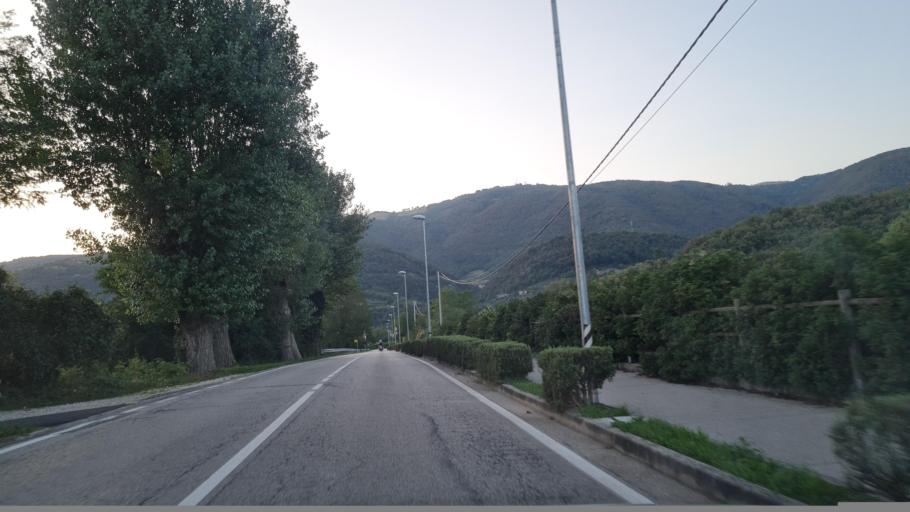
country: IT
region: Veneto
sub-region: Provincia di Vicenza
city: Bassano del Grappa
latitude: 45.7710
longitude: 11.6956
